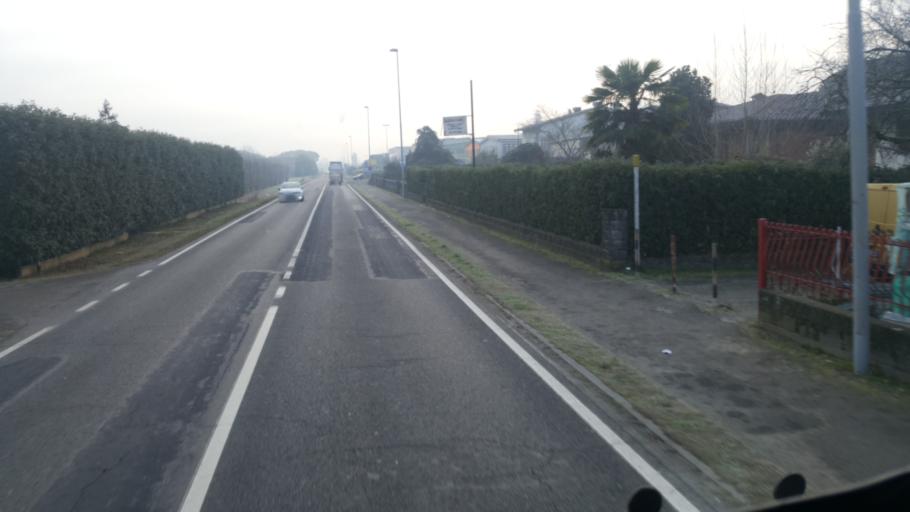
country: IT
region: Emilia-Romagna
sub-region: Provincia di Ravenna
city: Bagnacavallo
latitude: 44.4111
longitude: 11.9906
